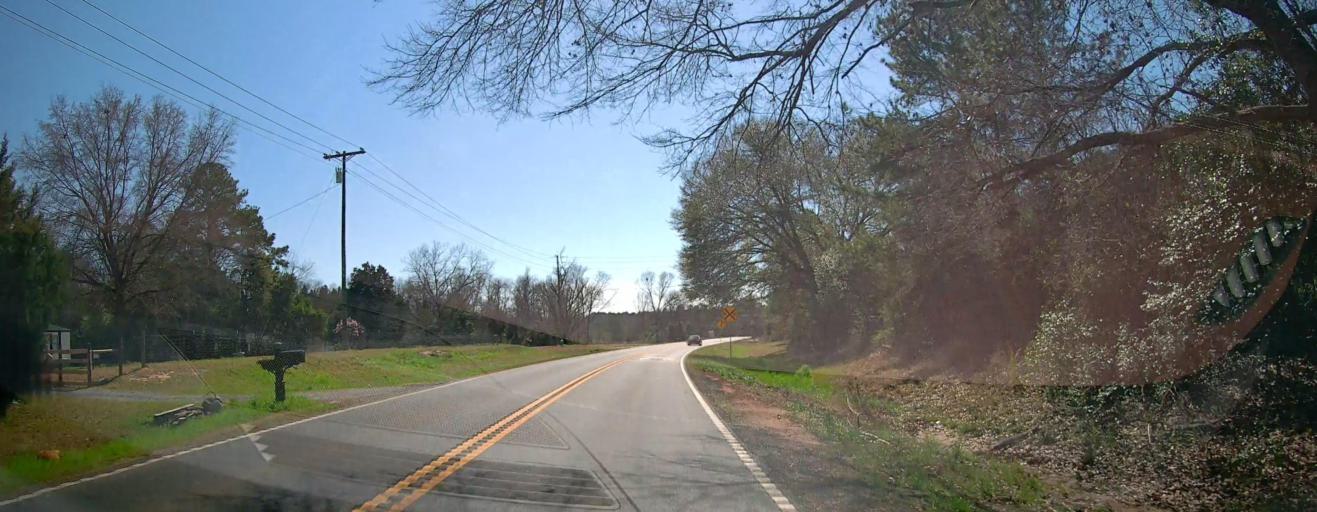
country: US
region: Georgia
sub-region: Houston County
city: Perry
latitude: 32.4564
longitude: -83.6190
